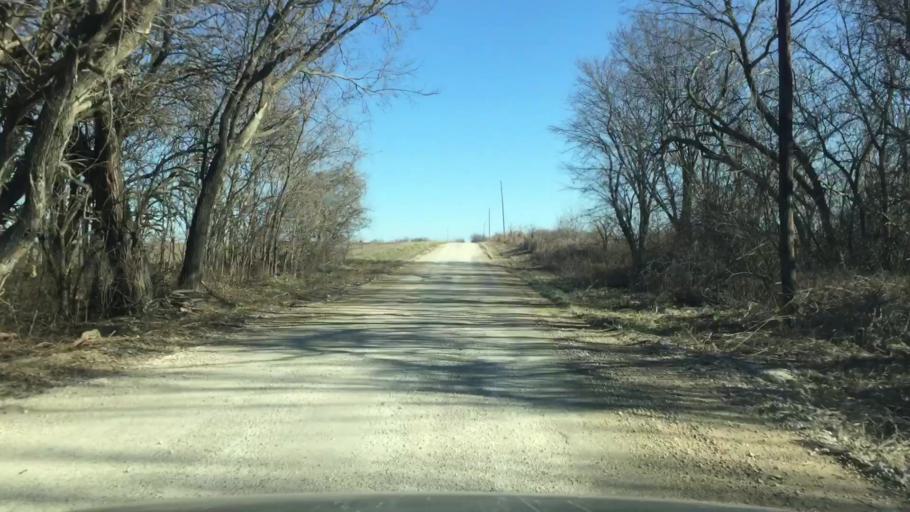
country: US
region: Kansas
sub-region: Allen County
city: Humboldt
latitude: 37.8493
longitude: -95.3977
